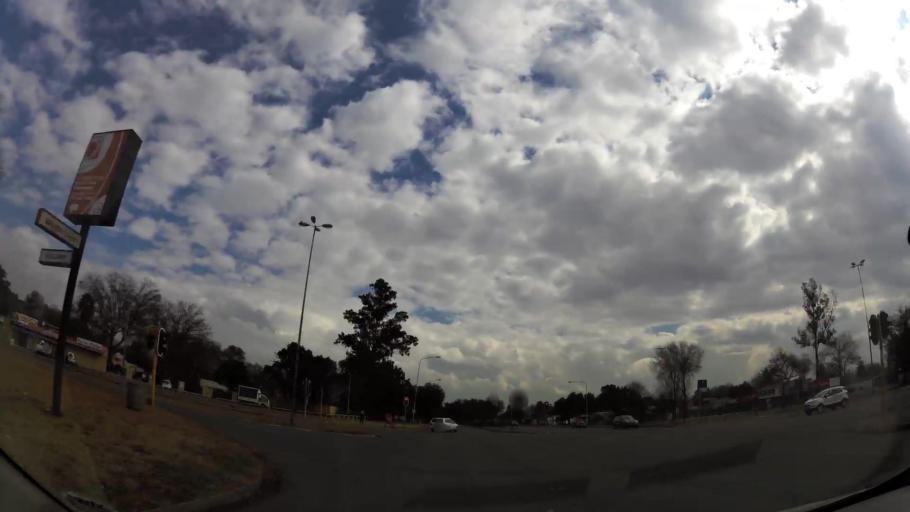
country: ZA
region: Gauteng
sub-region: Sedibeng District Municipality
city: Vereeniging
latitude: -26.6582
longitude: 27.9659
